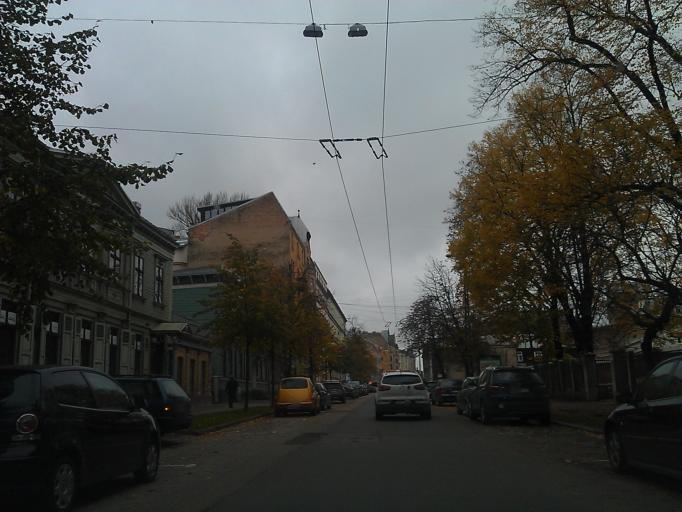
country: LV
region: Riga
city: Riga
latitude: 56.9577
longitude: 24.1290
